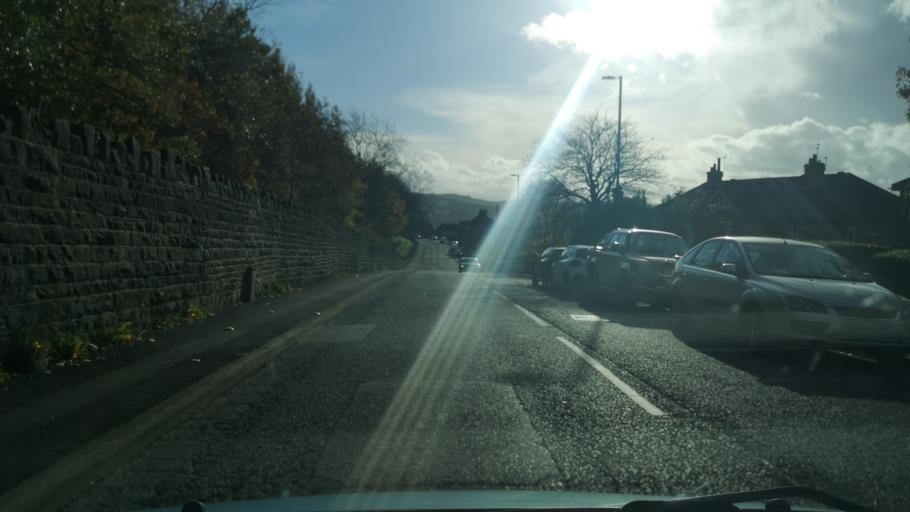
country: GB
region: England
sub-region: Kirklees
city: Batley
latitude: 53.6924
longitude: -1.6528
